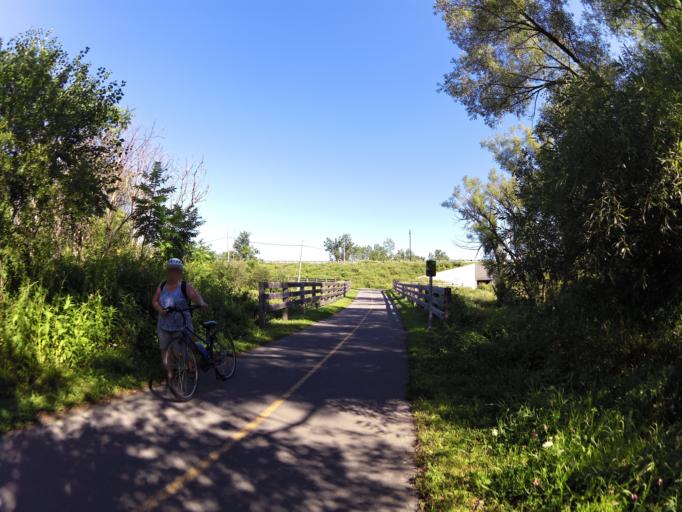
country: CA
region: Quebec
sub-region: Outaouais
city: Gatineau
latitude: 45.4623
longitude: -75.7281
